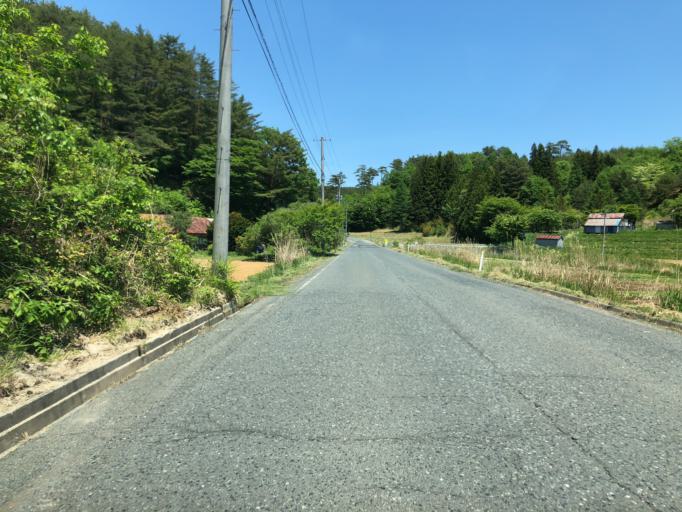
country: JP
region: Fukushima
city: Funehikimachi-funehiki
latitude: 37.5188
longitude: 140.7768
